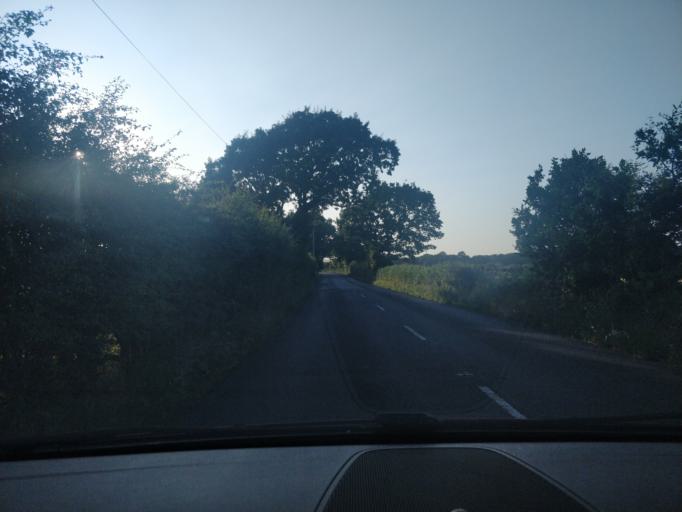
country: GB
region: England
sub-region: Lancashire
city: Parbold
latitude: 53.6051
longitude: -2.7711
